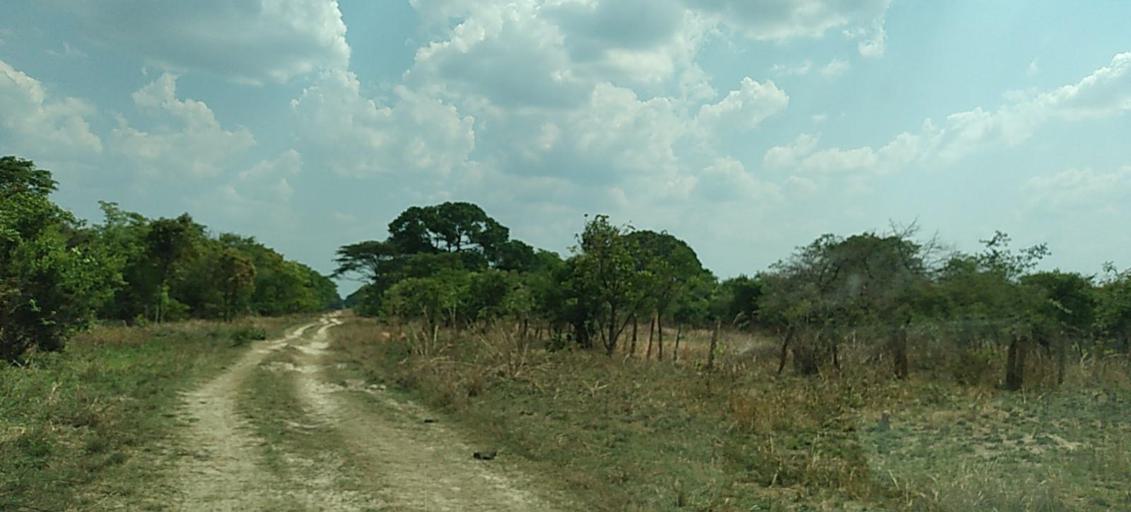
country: ZM
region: Copperbelt
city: Mpongwe
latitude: -13.8342
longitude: 27.9384
